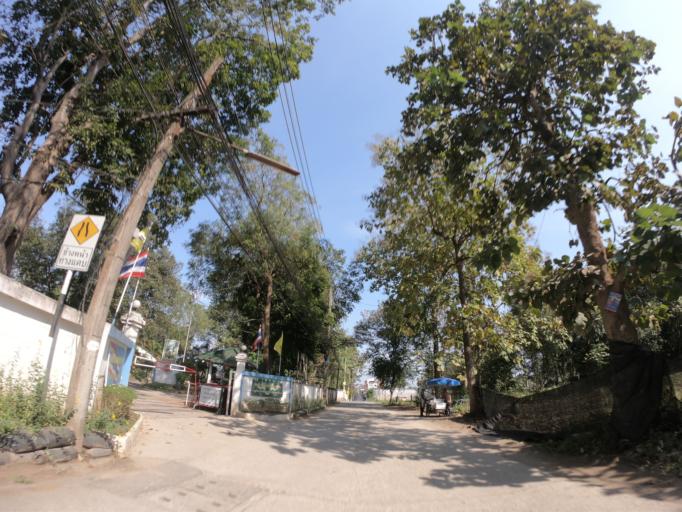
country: TH
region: Chiang Mai
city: Chiang Mai
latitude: 18.8235
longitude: 98.9842
